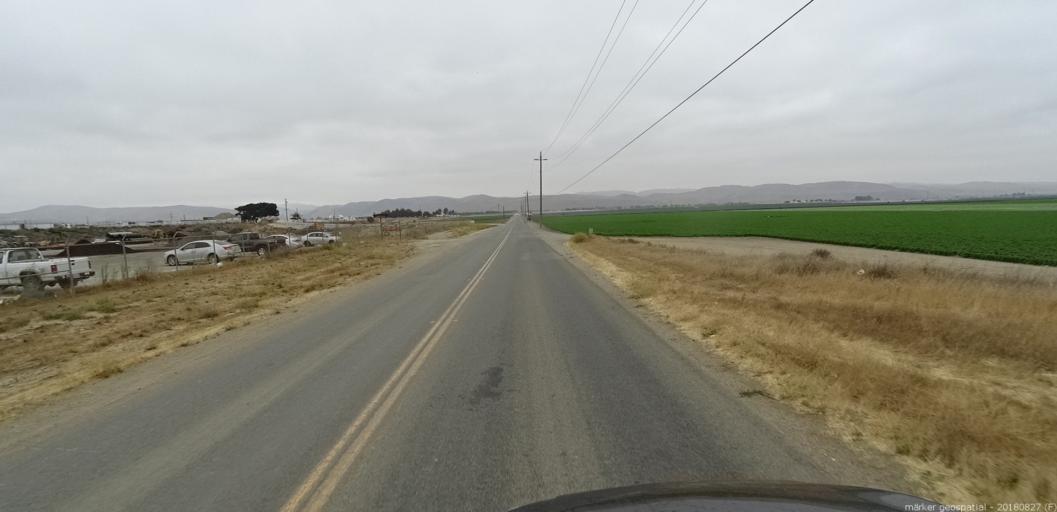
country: US
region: California
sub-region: Monterey County
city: Greenfield
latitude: 36.3238
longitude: -121.2299
